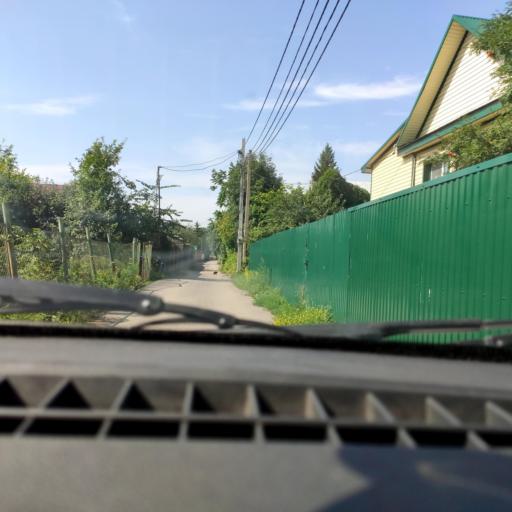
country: RU
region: Bashkortostan
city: Ufa
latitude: 54.6756
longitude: 56.0084
